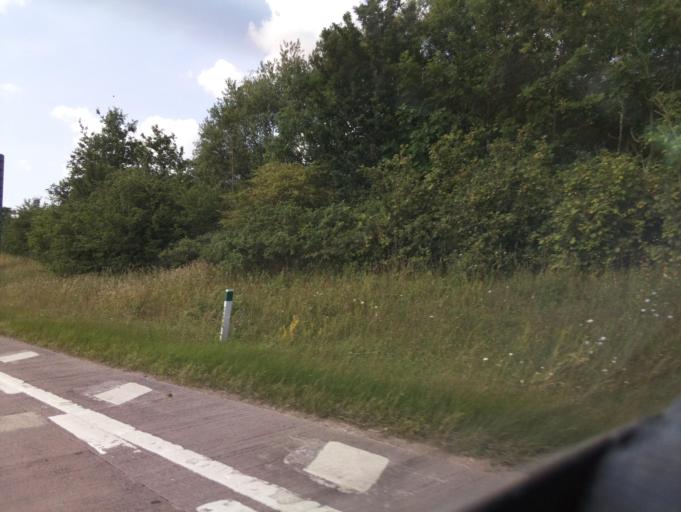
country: GB
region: England
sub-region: Wiltshire
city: Cricklade
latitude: 51.6780
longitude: -1.8970
